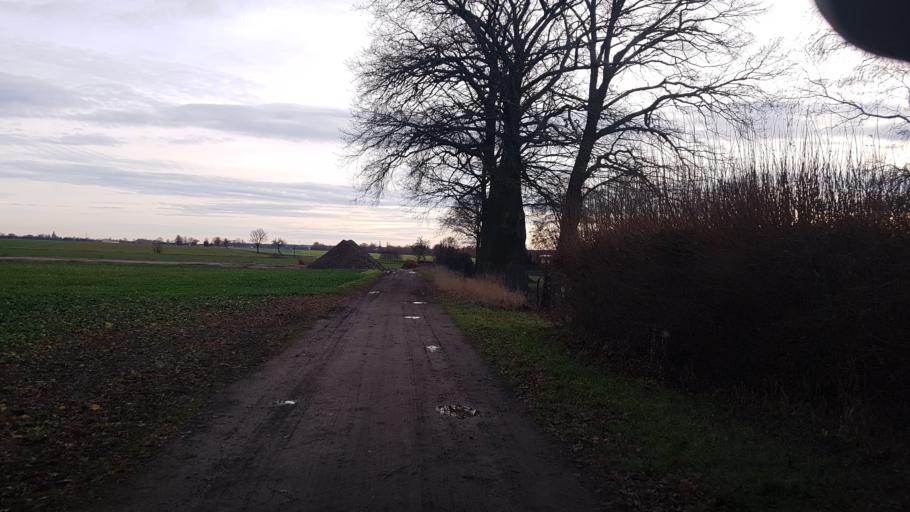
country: DE
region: Brandenburg
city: Doberlug-Kirchhain
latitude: 51.6709
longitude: 13.5132
